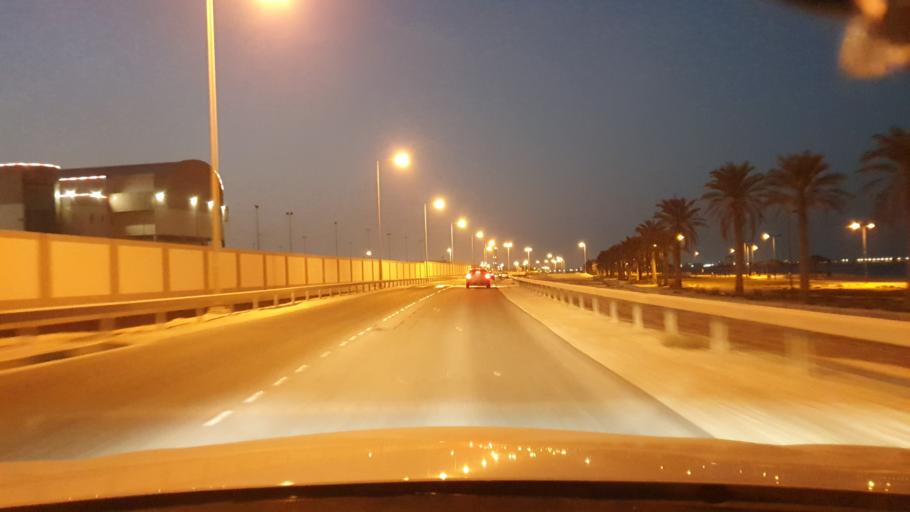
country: BH
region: Northern
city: Ar Rifa'
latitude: 26.0453
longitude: 50.6203
